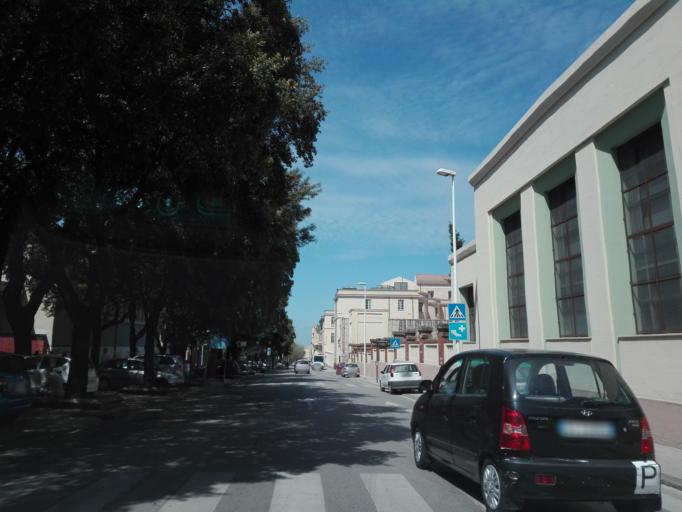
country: IT
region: Sardinia
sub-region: Provincia di Sassari
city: Sassari
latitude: 40.7216
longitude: 8.5637
